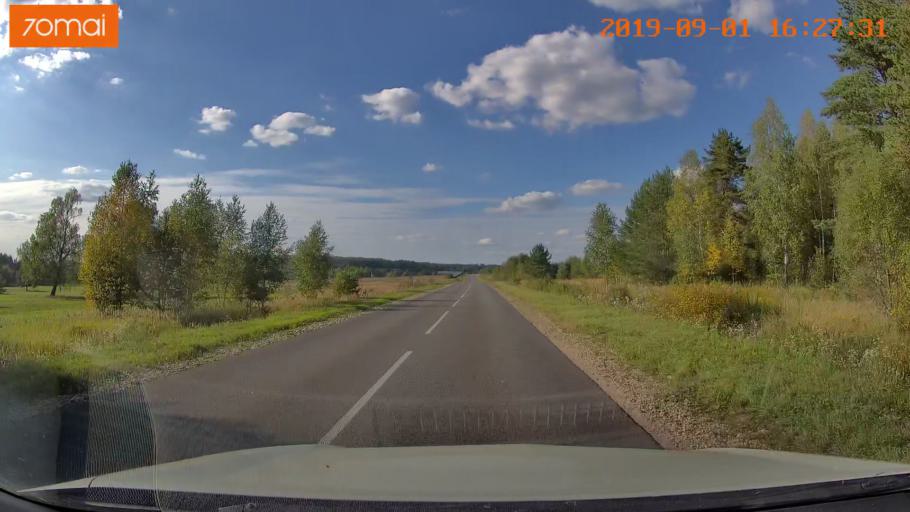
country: RU
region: Kaluga
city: Maloyaroslavets
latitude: 54.9166
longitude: 36.4828
